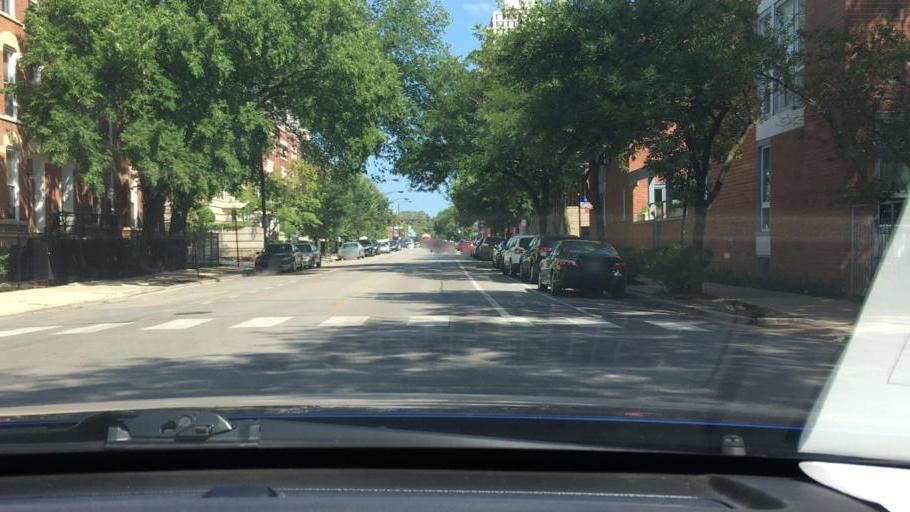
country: US
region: Illinois
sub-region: Cook County
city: Chicago
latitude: 41.9183
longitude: -87.6412
